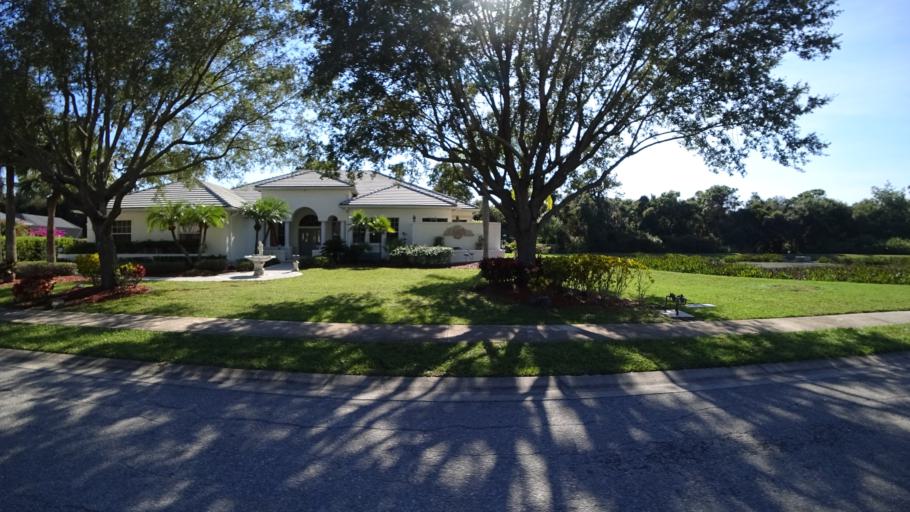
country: US
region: Florida
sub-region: Sarasota County
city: The Meadows
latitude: 27.4041
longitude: -82.4386
